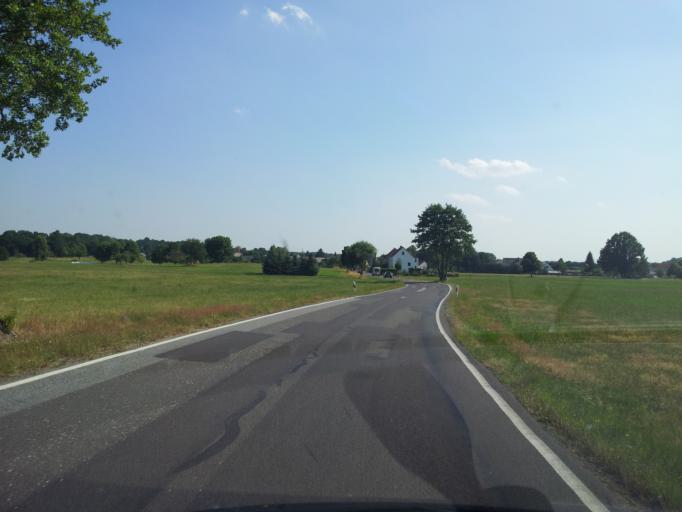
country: DE
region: Saxony
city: Hockendorf
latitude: 51.2289
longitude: 13.9084
